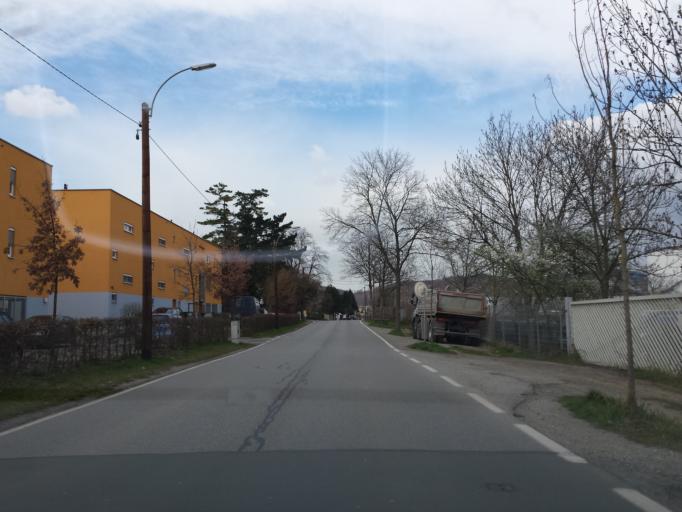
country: AT
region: Styria
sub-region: Graz Stadt
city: Goesting
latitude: 47.0867
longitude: 15.4047
